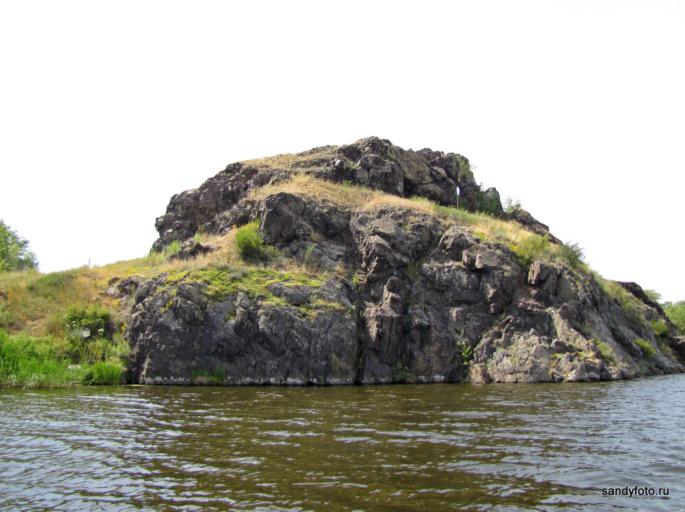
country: RU
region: Chelyabinsk
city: Troitsk
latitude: 54.0717
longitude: 61.5805
